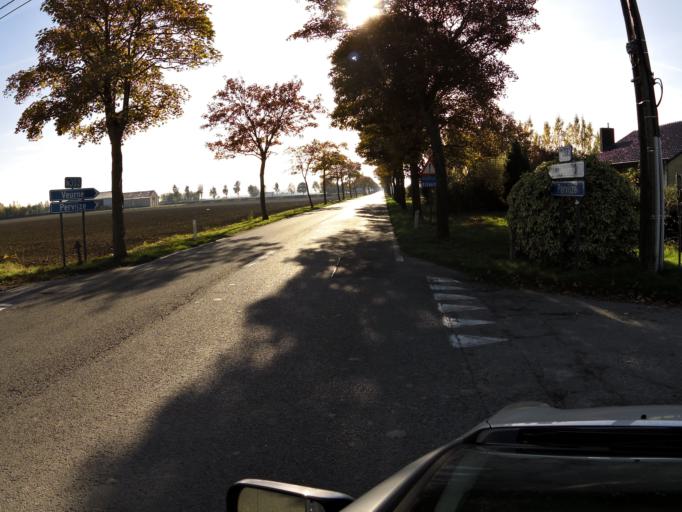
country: BE
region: Flanders
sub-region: Provincie West-Vlaanderen
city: Nieuwpoort
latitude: 51.0967
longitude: 2.8198
